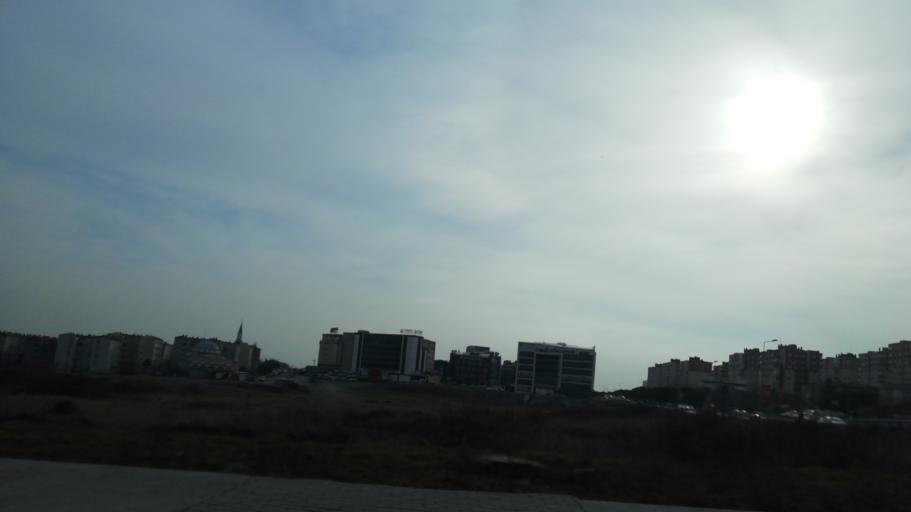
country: TR
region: Istanbul
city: Basaksehir
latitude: 41.1074
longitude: 28.7955
